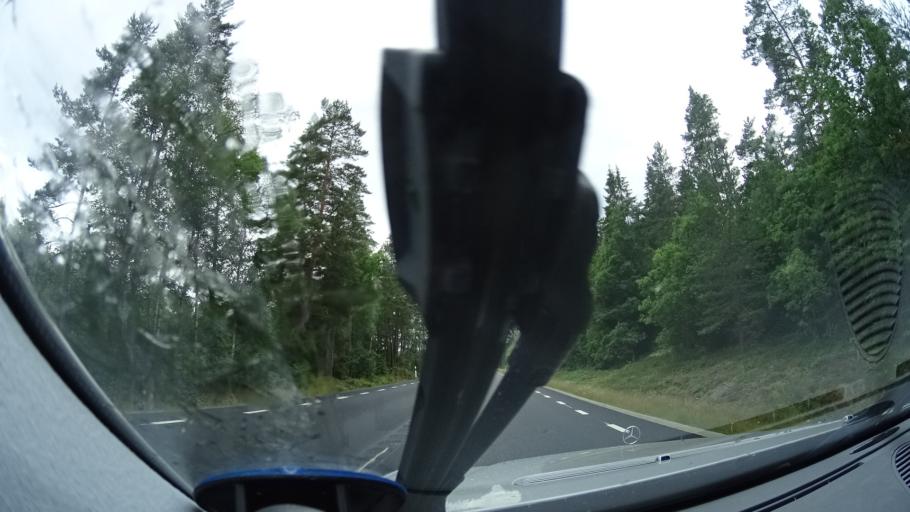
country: SE
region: Kronoberg
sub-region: Tingsryds Kommun
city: Tingsryd
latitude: 56.4048
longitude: 14.9311
